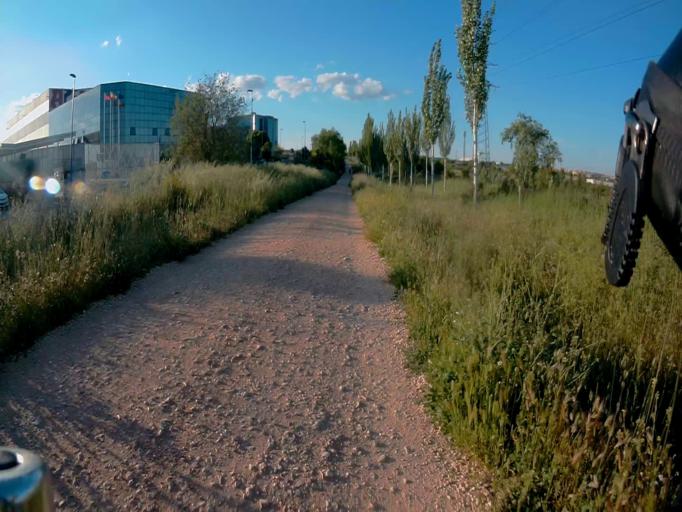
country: ES
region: Madrid
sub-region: Provincia de Madrid
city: Fuenlabrada
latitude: 40.3080
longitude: -3.7983
